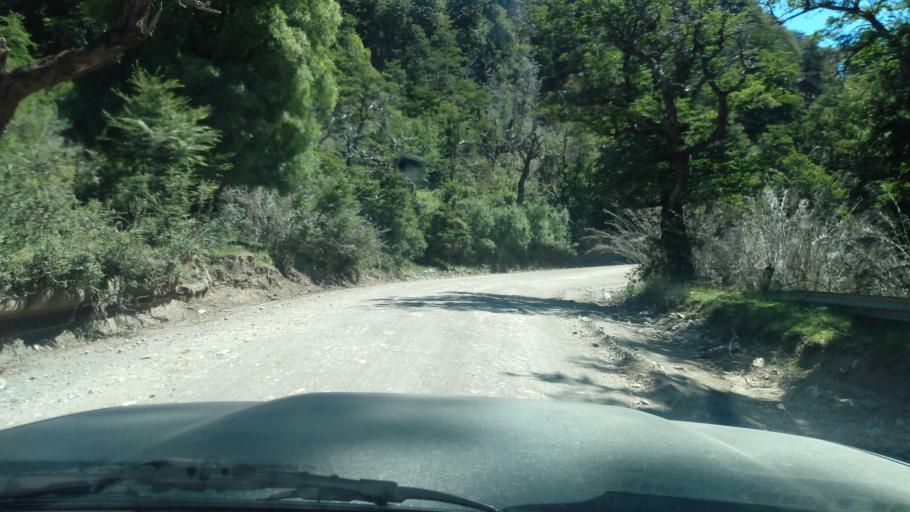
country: AR
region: Neuquen
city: Villa La Angostura
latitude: -40.6049
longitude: -71.6184
